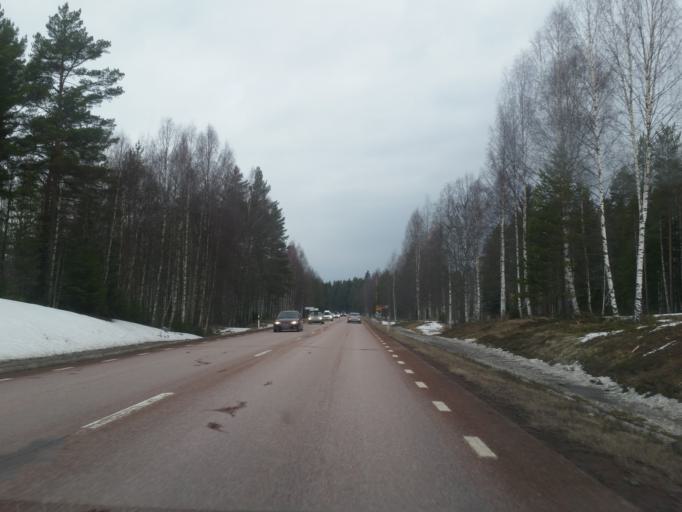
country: SE
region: Dalarna
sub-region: Alvdalens Kommun
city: AElvdalen
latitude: 61.1206
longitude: 14.2398
